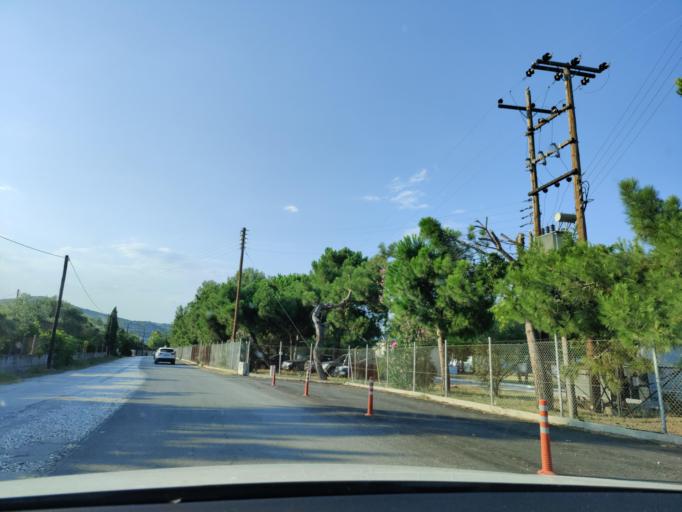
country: GR
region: East Macedonia and Thrace
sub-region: Nomos Kavalas
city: Nea Peramos
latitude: 40.8284
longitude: 24.3053
